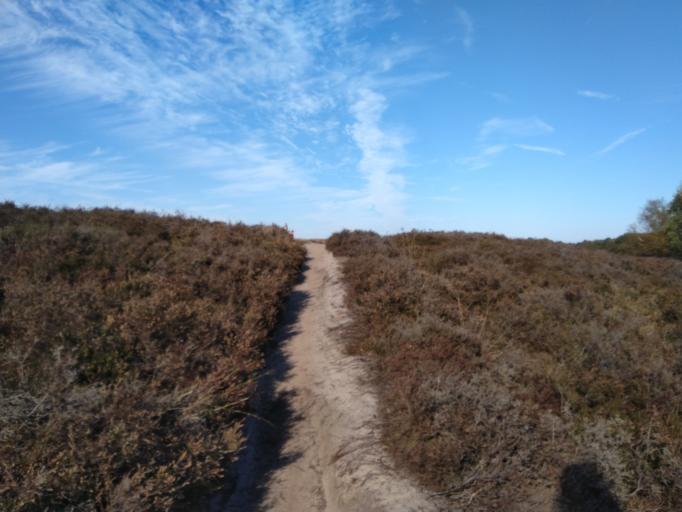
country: NL
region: Drenthe
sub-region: Gemeente Aa en Hunze
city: Anloo
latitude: 53.0438
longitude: 6.6579
